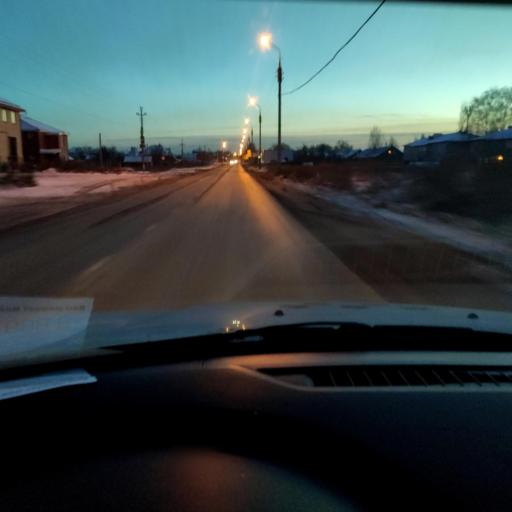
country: RU
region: Samara
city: Tol'yatti
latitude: 53.5658
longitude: 49.3967
